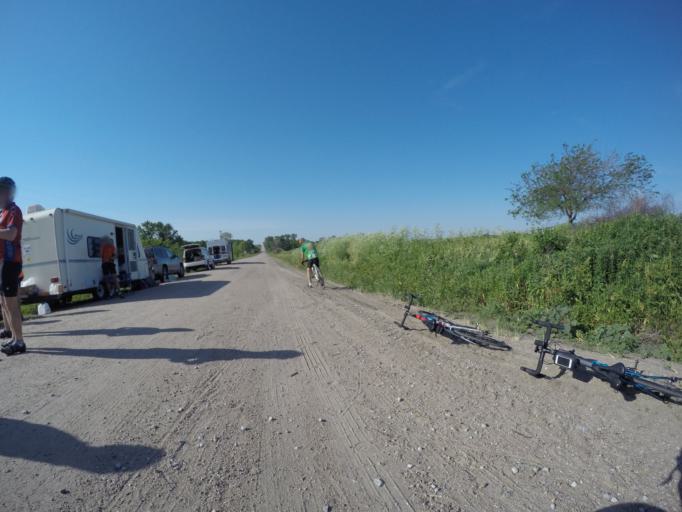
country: US
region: Nebraska
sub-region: Gage County
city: Wymore
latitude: 40.0445
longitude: -96.4829
